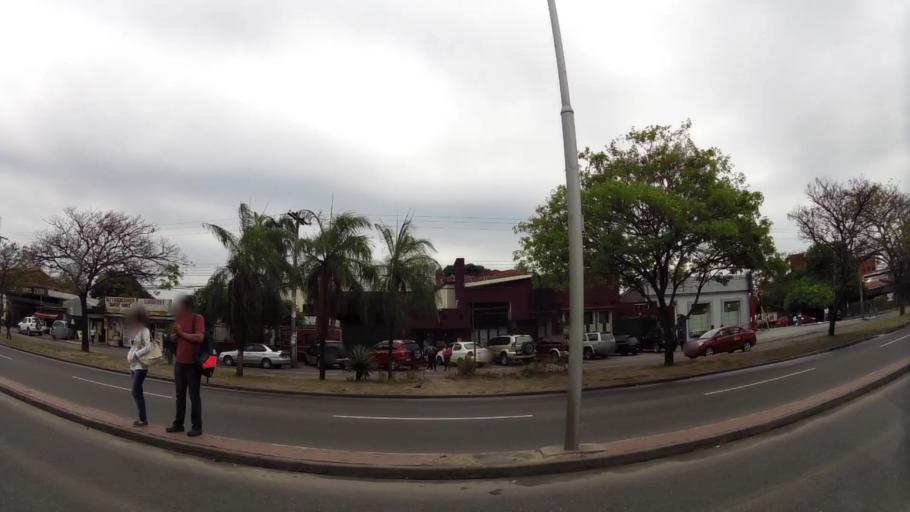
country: BO
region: Santa Cruz
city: Santa Cruz de la Sierra
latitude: -17.7887
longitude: -63.1648
